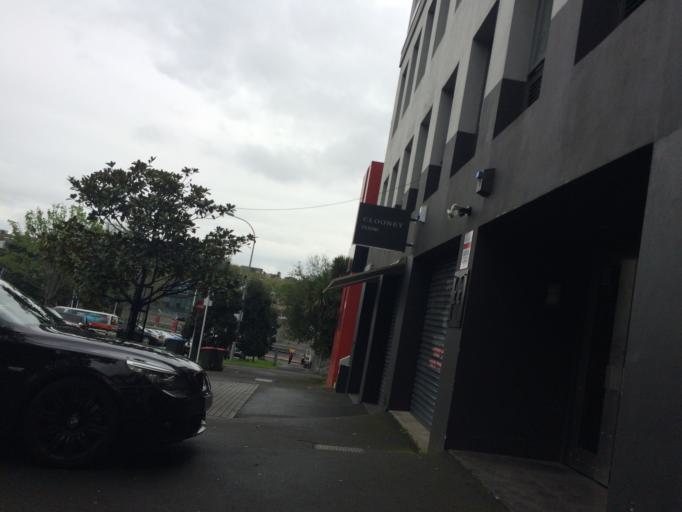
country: NZ
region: Auckland
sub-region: Auckland
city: Auckland
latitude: -36.8495
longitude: 174.7549
